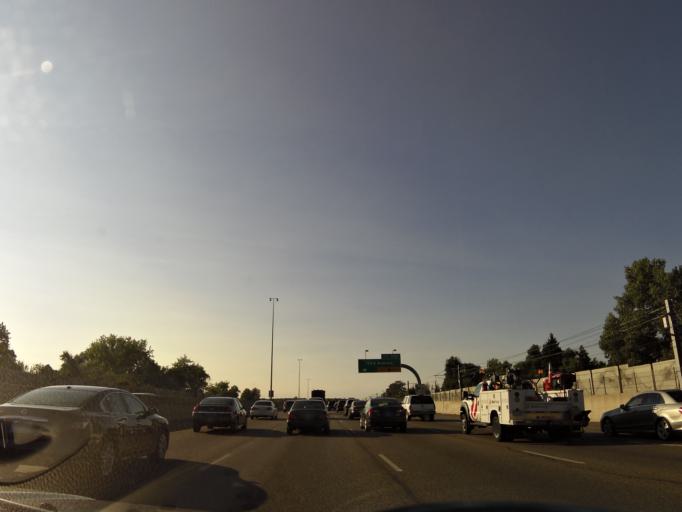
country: US
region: Colorado
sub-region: Arapahoe County
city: Glendale
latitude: 39.6728
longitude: -104.9290
